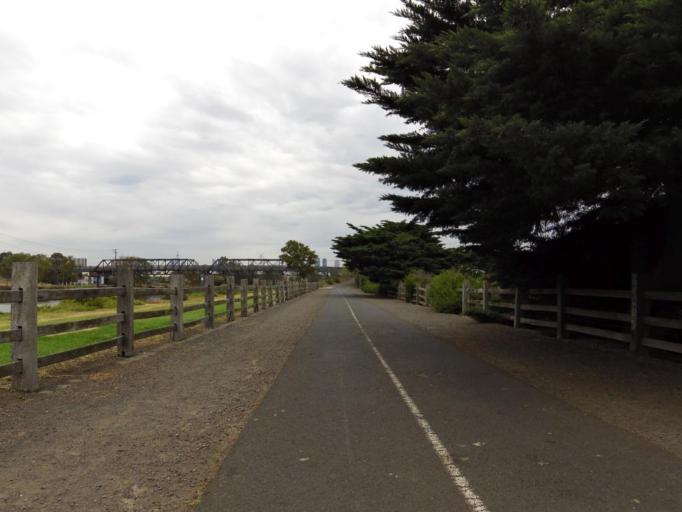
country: AU
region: Victoria
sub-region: Melbourne
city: Ascot Vale
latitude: -37.7959
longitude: 144.9134
